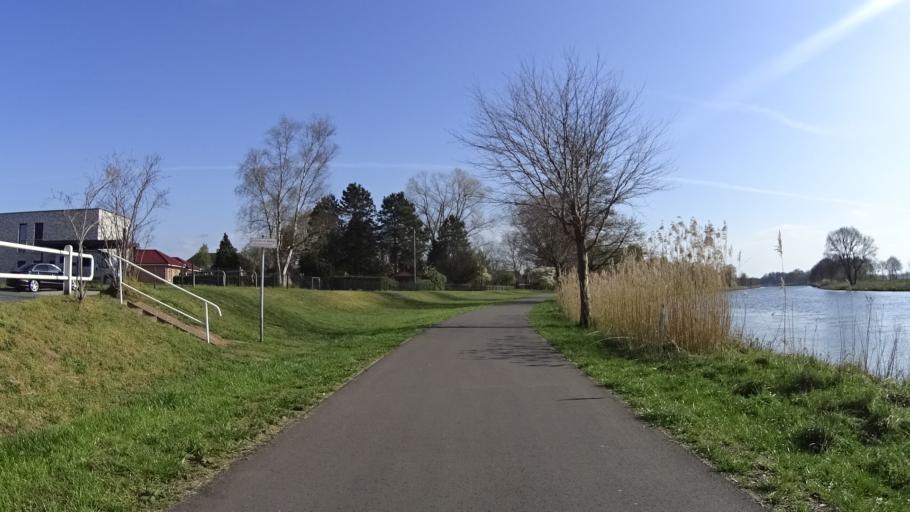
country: DE
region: Lower Saxony
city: Walchum
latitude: 52.9240
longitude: 7.3024
